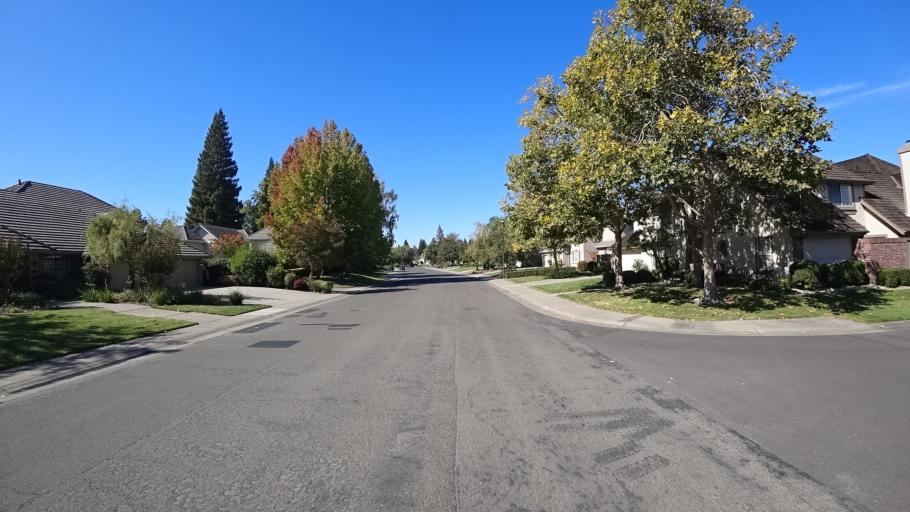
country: US
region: California
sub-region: Sacramento County
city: Parkway
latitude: 38.4786
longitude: -121.5281
